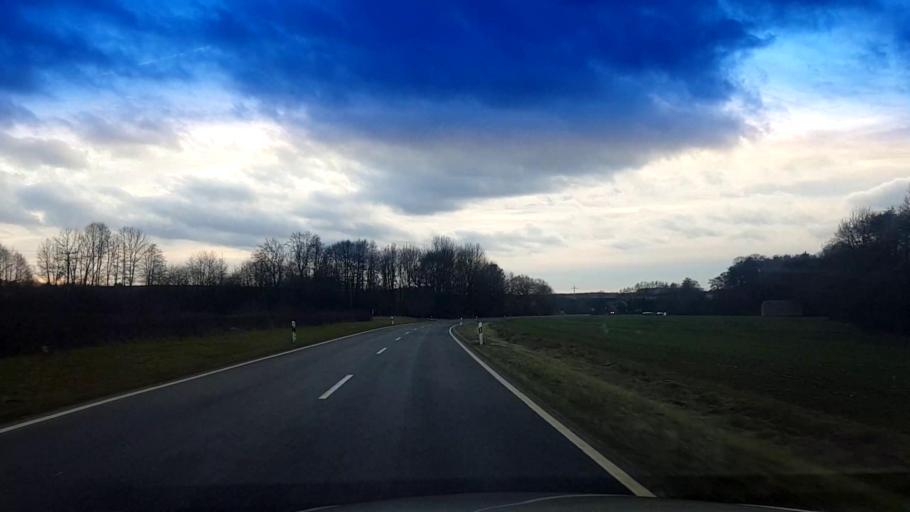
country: DE
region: Bavaria
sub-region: Upper Franconia
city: Strullendorf
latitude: 49.8618
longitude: 11.0163
